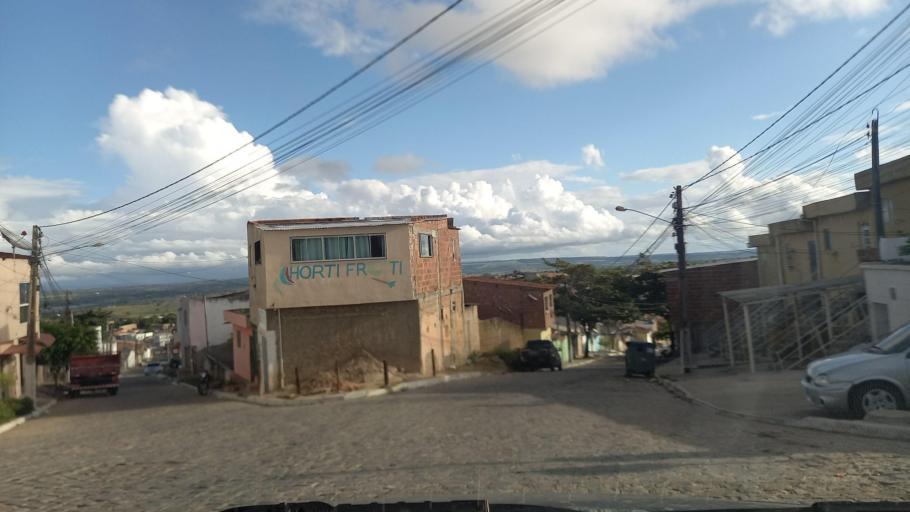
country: BR
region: Pernambuco
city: Garanhuns
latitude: -8.8992
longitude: -36.4984
